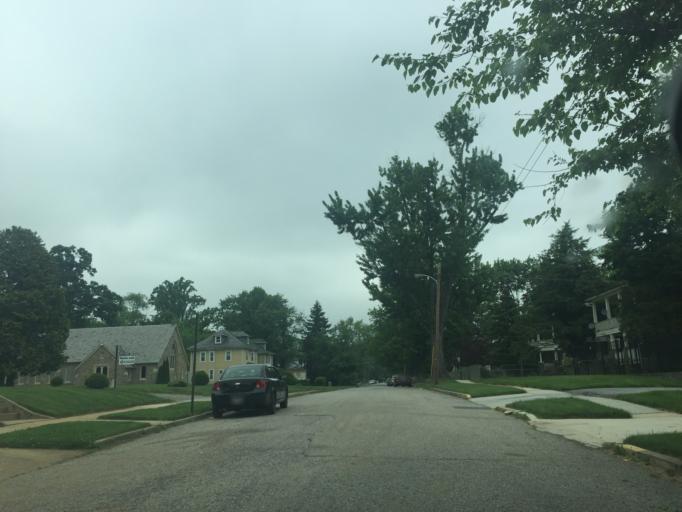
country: US
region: Maryland
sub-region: Baltimore County
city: Lochearn
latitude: 39.3310
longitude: -76.6928
